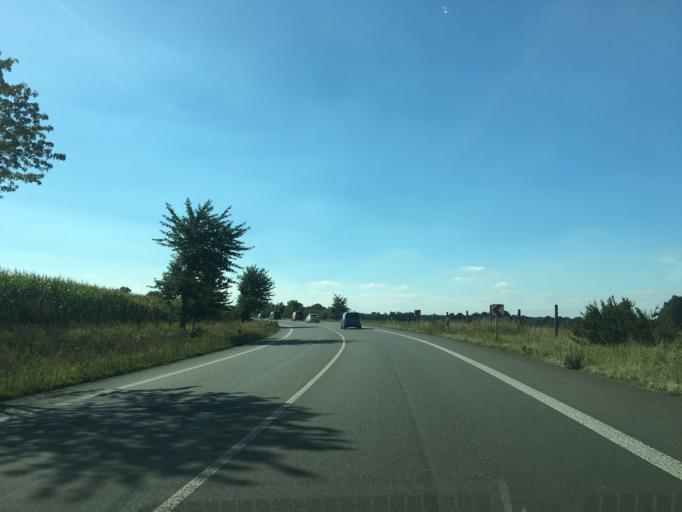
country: DE
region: North Rhine-Westphalia
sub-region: Regierungsbezirk Detmold
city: Rheda-Wiedenbruck
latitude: 51.8810
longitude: 8.2949
